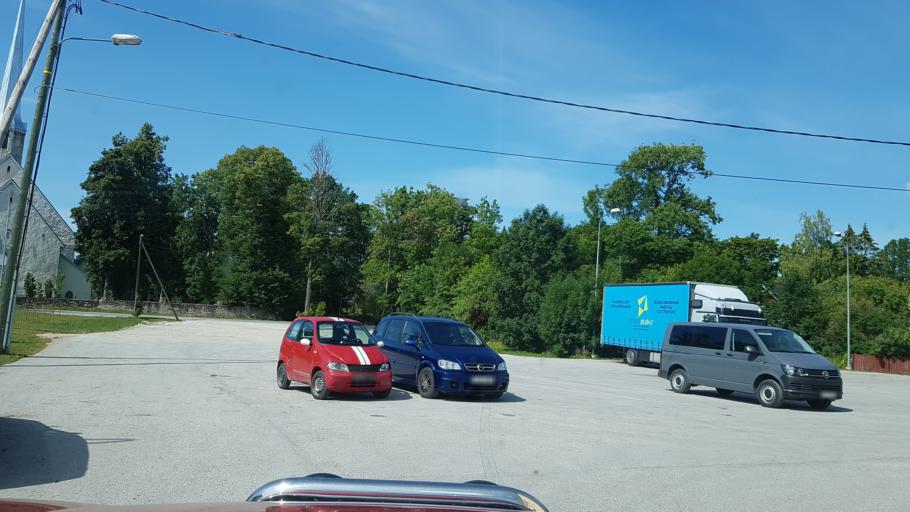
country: EE
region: Laeaene-Virumaa
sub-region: Vaeike-Maarja vald
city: Vaike-Maarja
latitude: 59.1300
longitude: 26.2517
